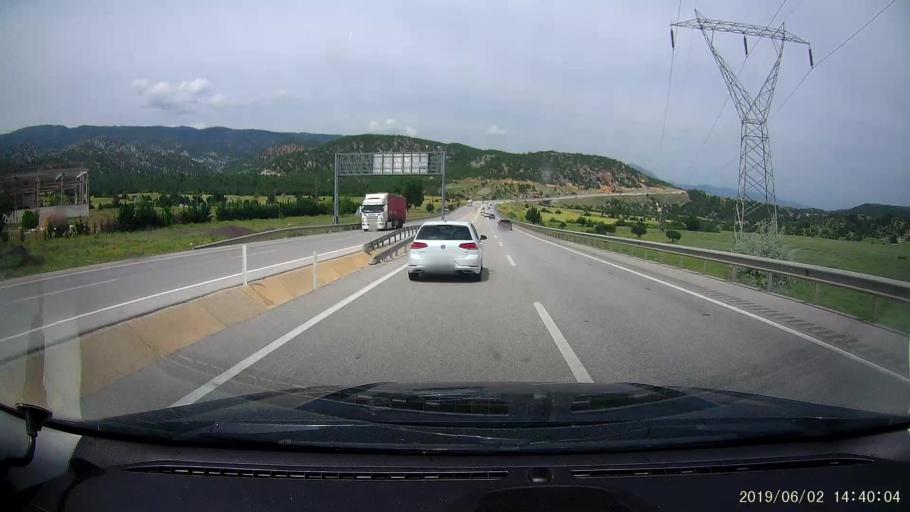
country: TR
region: Corum
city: Hacihamza
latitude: 41.0776
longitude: 34.3126
